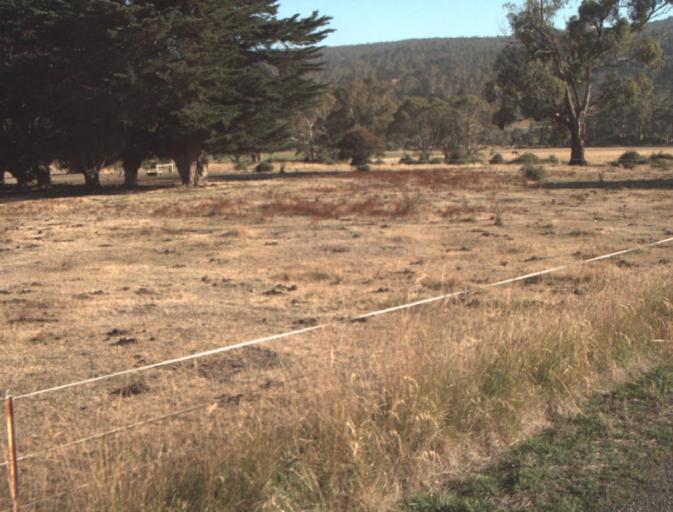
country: AU
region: Tasmania
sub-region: Launceston
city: Newstead
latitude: -41.4371
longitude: 147.2107
